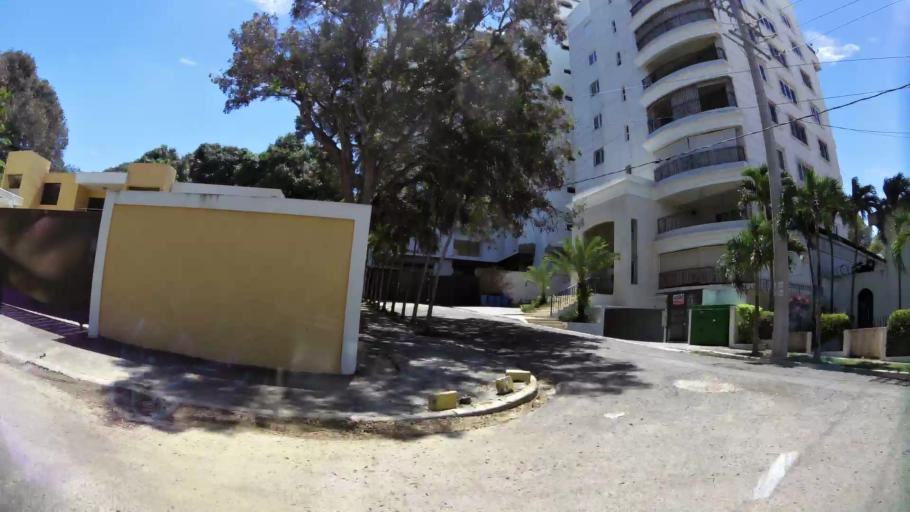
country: DO
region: Santiago
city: Santiago de los Caballeros
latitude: 19.4552
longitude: -70.6916
